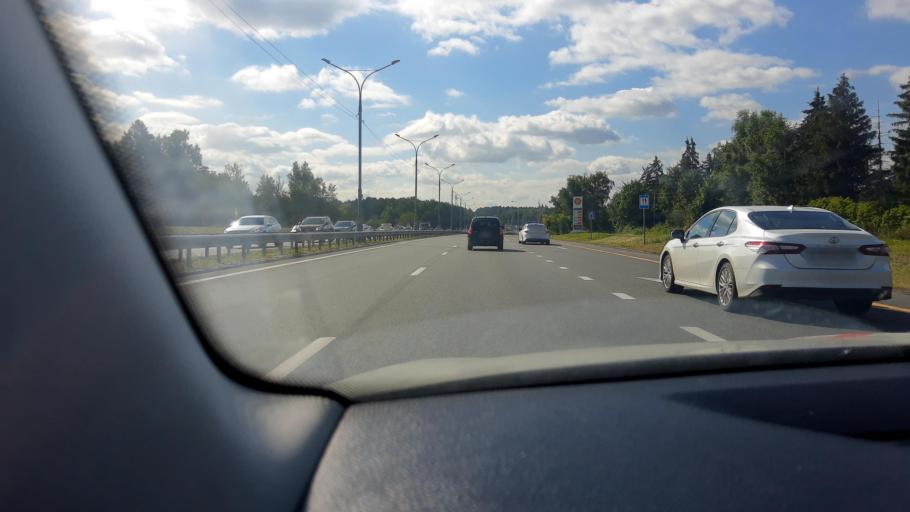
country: RU
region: Moskovskaya
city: Vostryakovo
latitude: 55.4715
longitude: 37.8528
